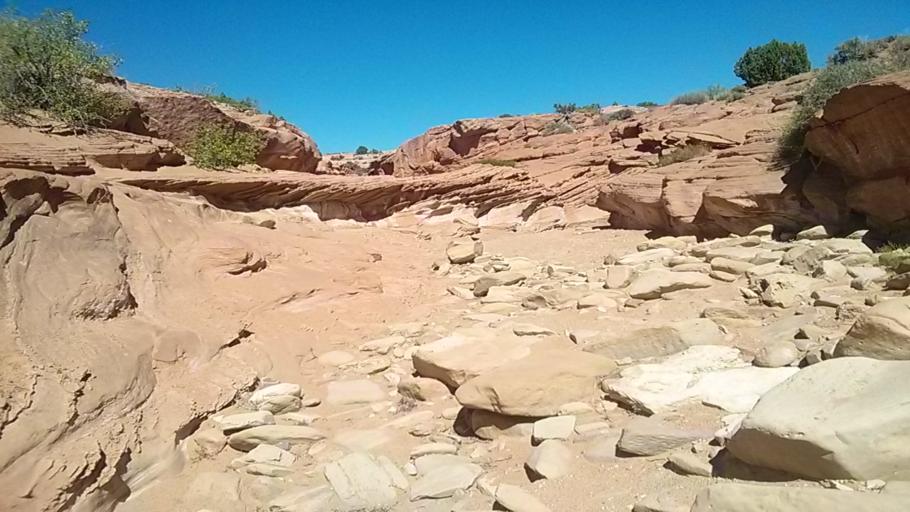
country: US
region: Arizona
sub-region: Coconino County
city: Page
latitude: 37.4826
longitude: -111.2281
